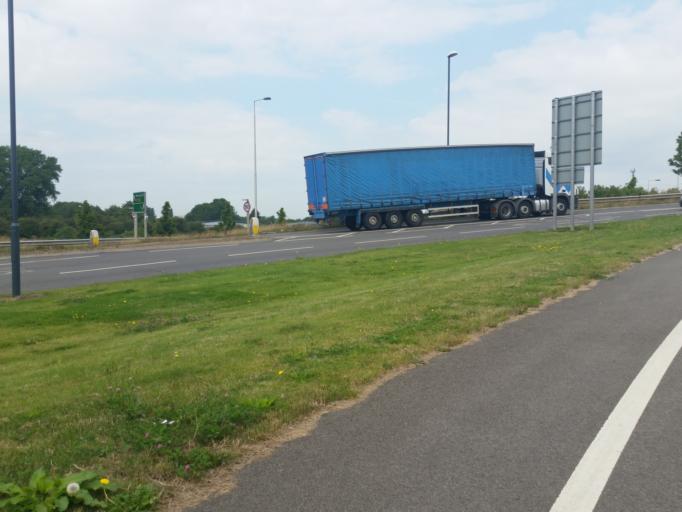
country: GB
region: England
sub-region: Derbyshire
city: Borrowash
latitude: 52.9007
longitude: -1.4265
